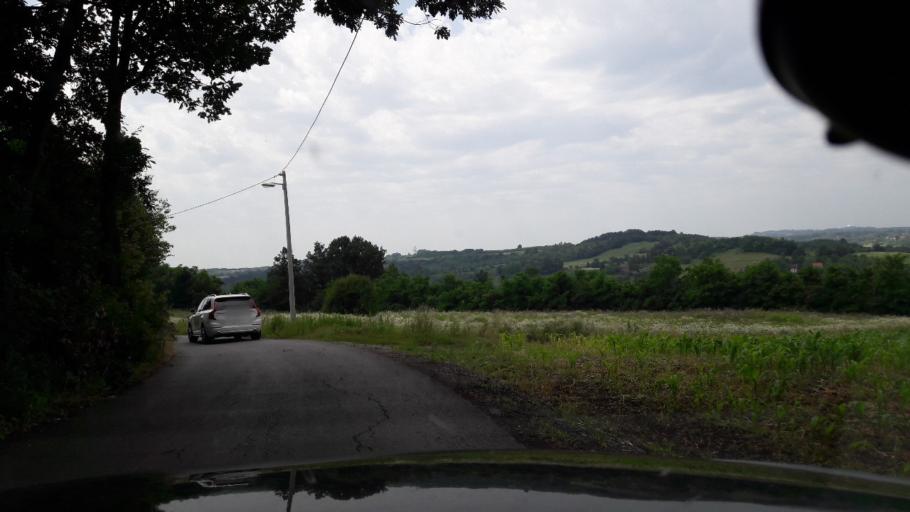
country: RS
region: Central Serbia
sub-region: Belgrade
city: Sopot
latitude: 44.6380
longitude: 20.5925
